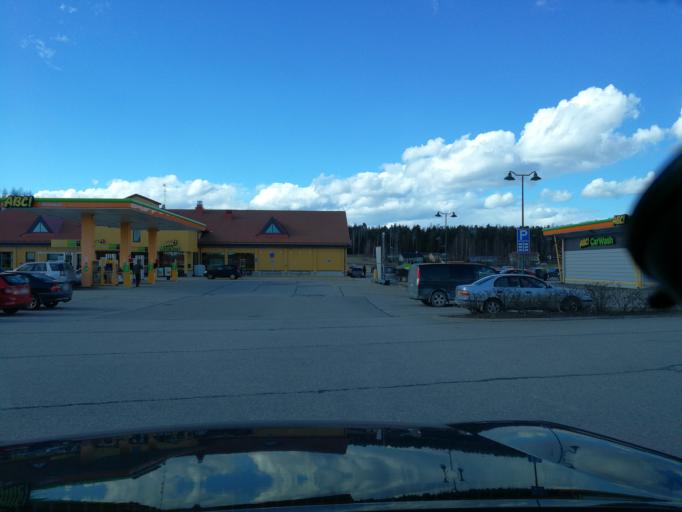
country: FI
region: Uusimaa
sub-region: Raaseporin
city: Karis
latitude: 60.0543
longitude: 23.6477
